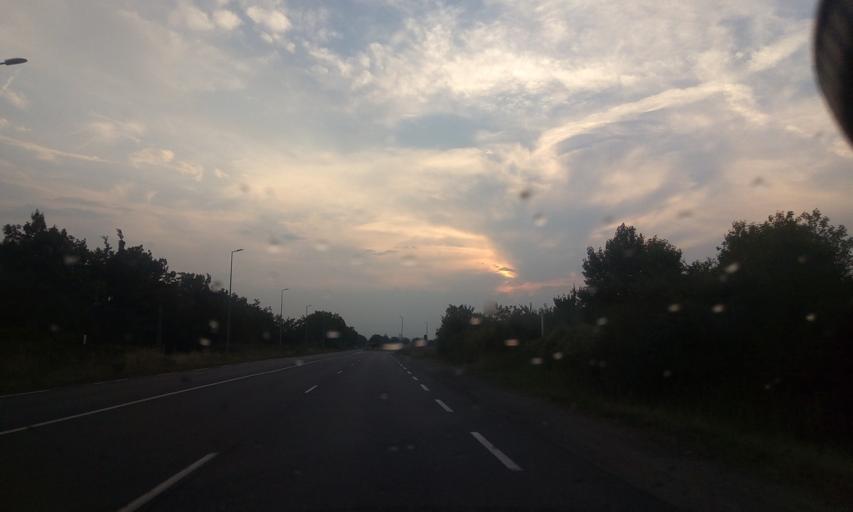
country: FR
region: Rhone-Alpes
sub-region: Departement du Rhone
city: Chassieu
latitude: 45.7417
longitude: 4.9456
